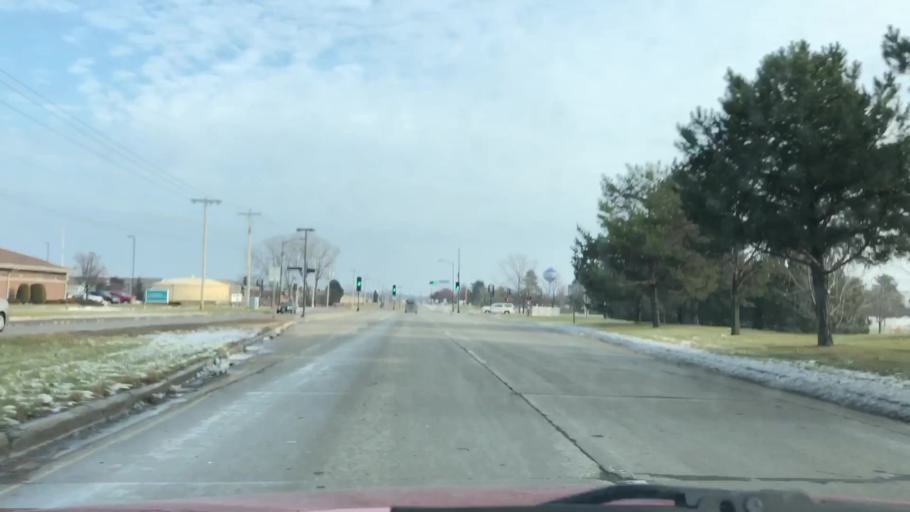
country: US
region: Wisconsin
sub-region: Brown County
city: De Pere
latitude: 44.4308
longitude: -88.1022
